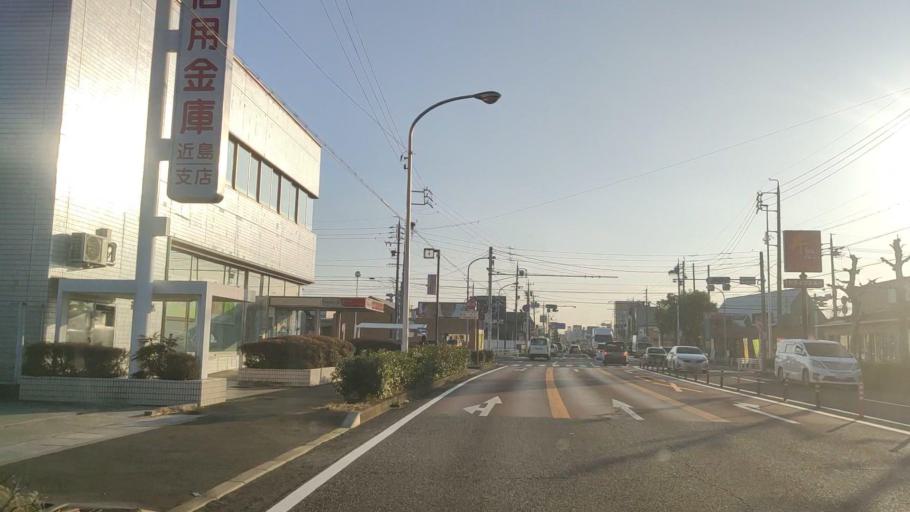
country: JP
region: Gifu
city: Gifu-shi
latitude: 35.4317
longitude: 136.7348
